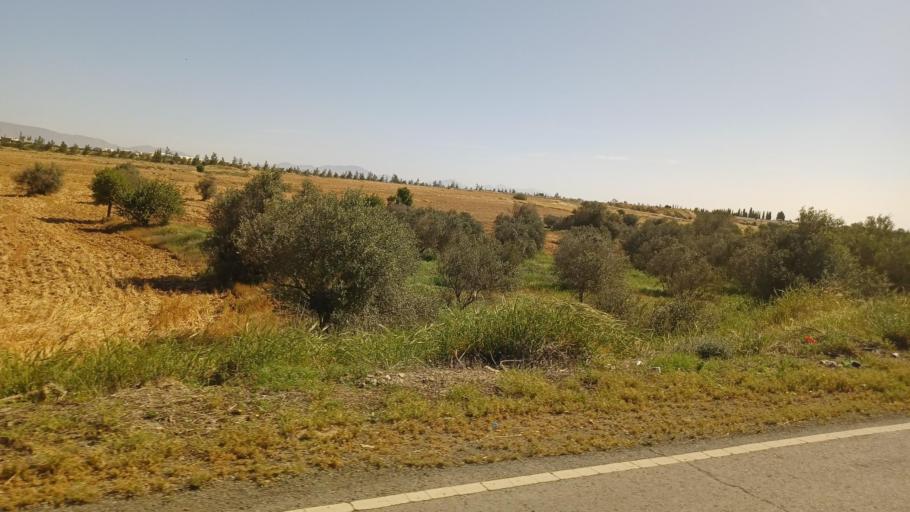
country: CY
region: Lefkosia
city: Kokkinotrimithia
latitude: 35.1570
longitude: 33.1852
